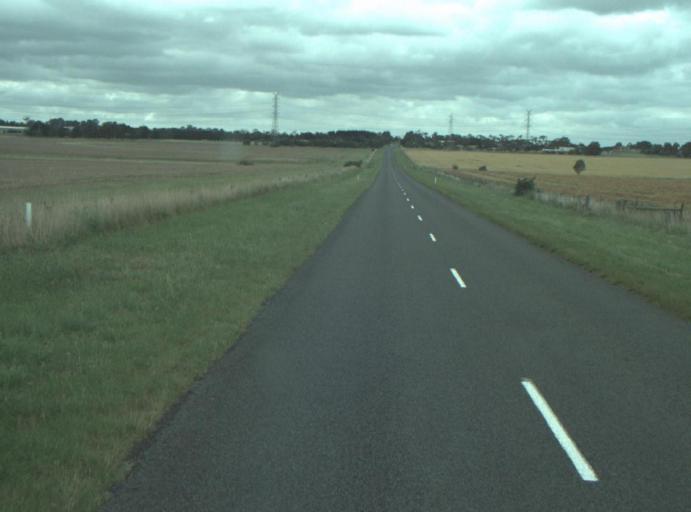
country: AU
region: Victoria
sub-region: Greater Geelong
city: Bell Post Hill
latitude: -38.0673
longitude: 144.3003
